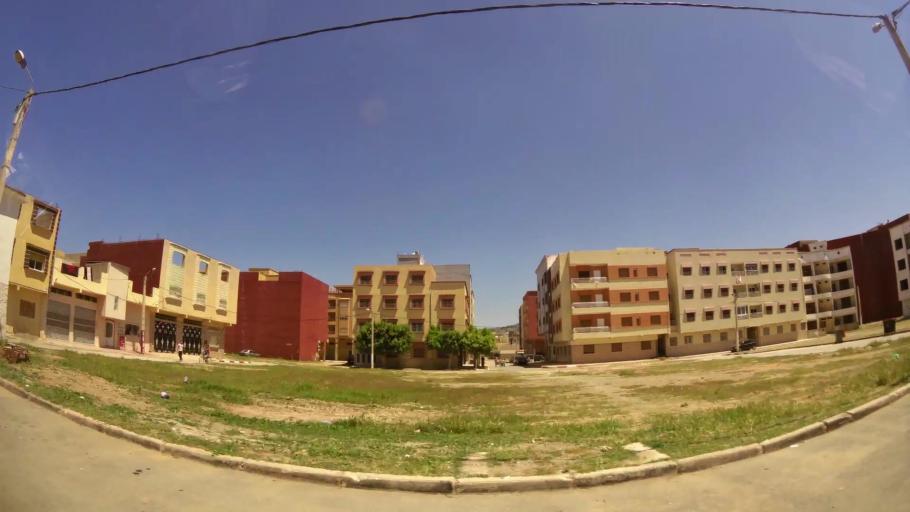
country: MA
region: Oriental
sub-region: Berkane-Taourirt
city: Madagh
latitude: 35.0773
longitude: -2.2247
